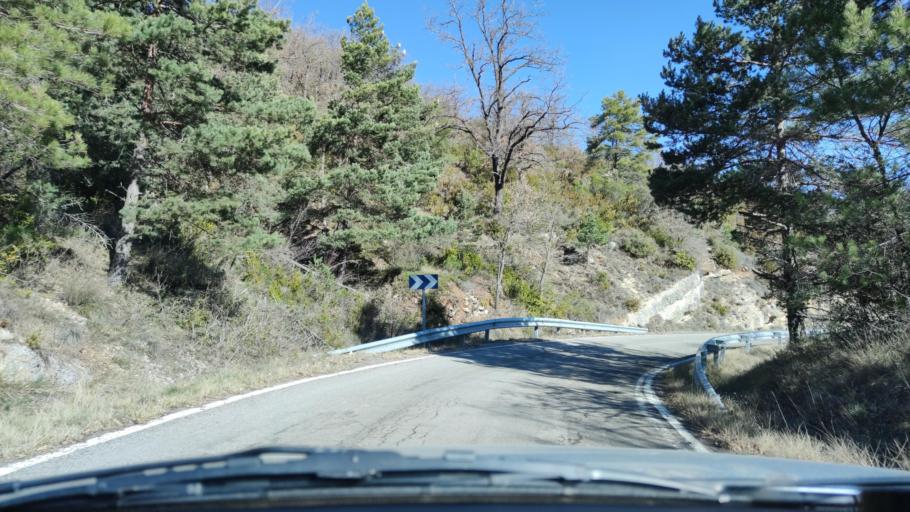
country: ES
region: Catalonia
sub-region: Provincia de Lleida
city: Llimiana
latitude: 42.0421
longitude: 1.0451
